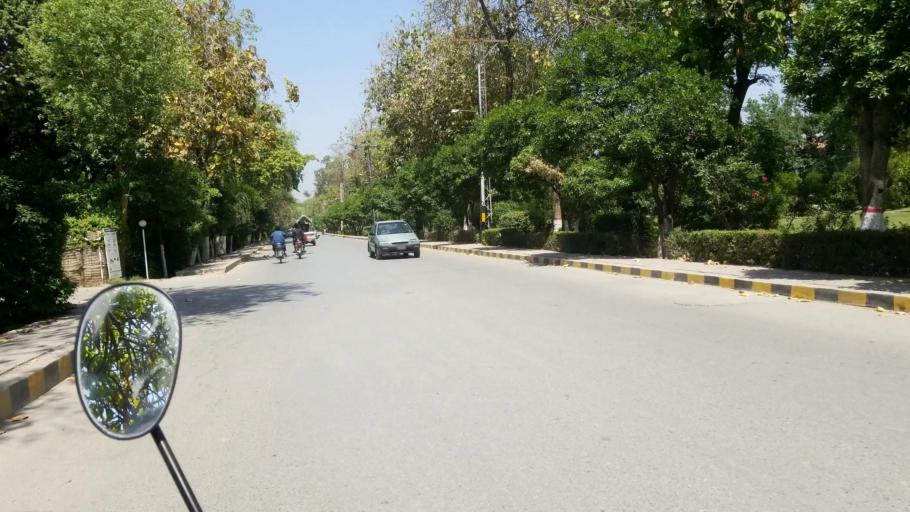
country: PK
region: Khyber Pakhtunkhwa
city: Peshawar
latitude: 34.0028
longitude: 71.4863
